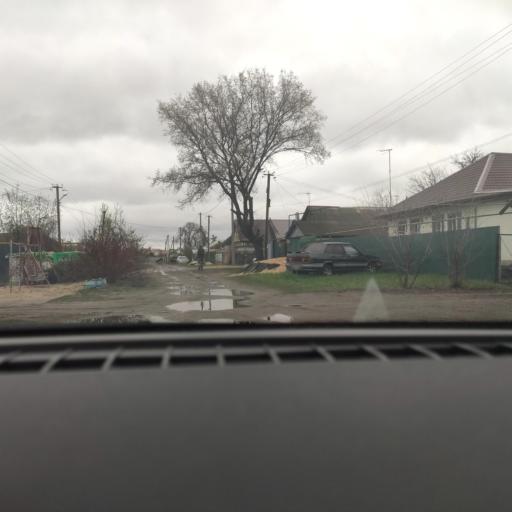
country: RU
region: Voronezj
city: Maslovka
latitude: 51.5339
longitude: 39.2300
